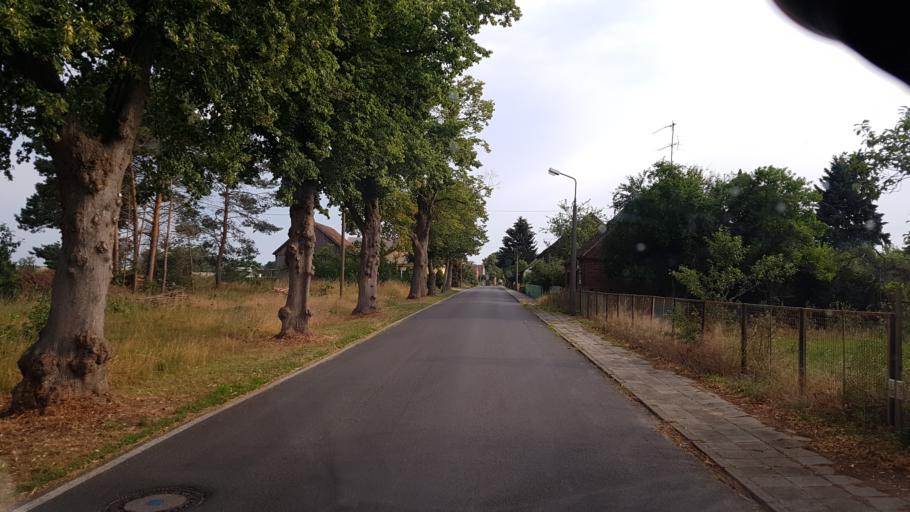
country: DE
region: Brandenburg
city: Dahme
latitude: 51.9426
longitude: 13.3957
